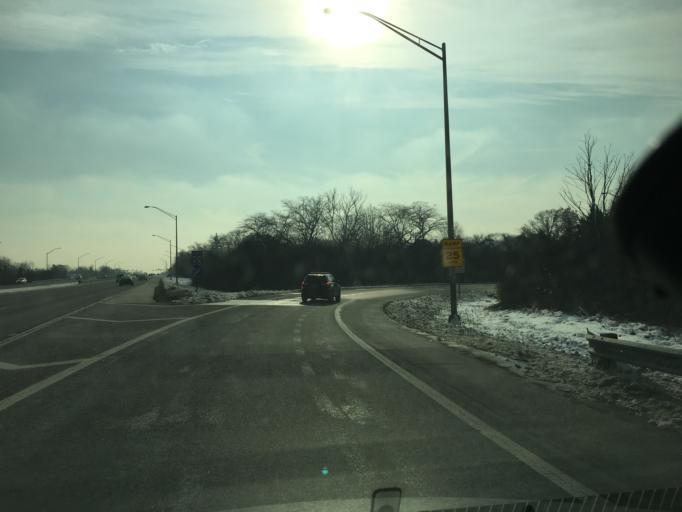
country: US
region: Illinois
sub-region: DuPage County
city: Burr Ridge
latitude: 41.7405
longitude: -87.9446
